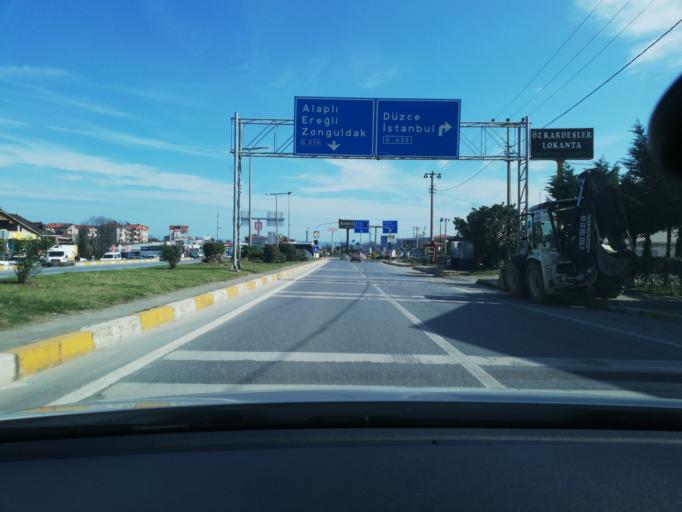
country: TR
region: Duzce
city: Akcakoca
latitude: 41.0848
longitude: 31.1748
